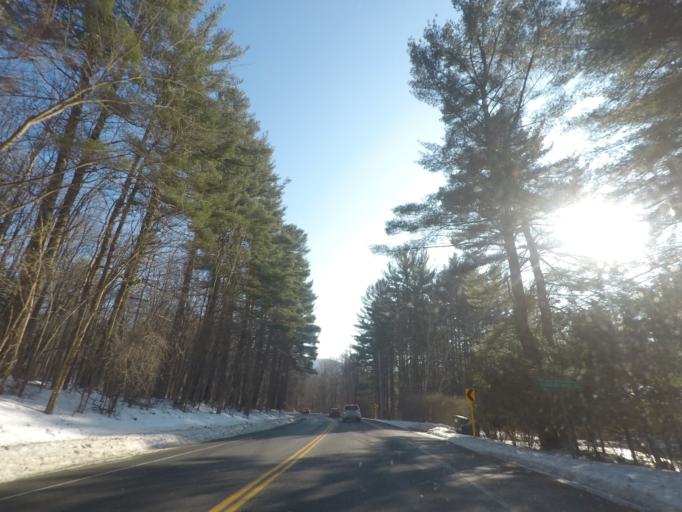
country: US
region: Massachusetts
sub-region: Berkshire County
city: Richmond
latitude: 42.4834
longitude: -73.3742
